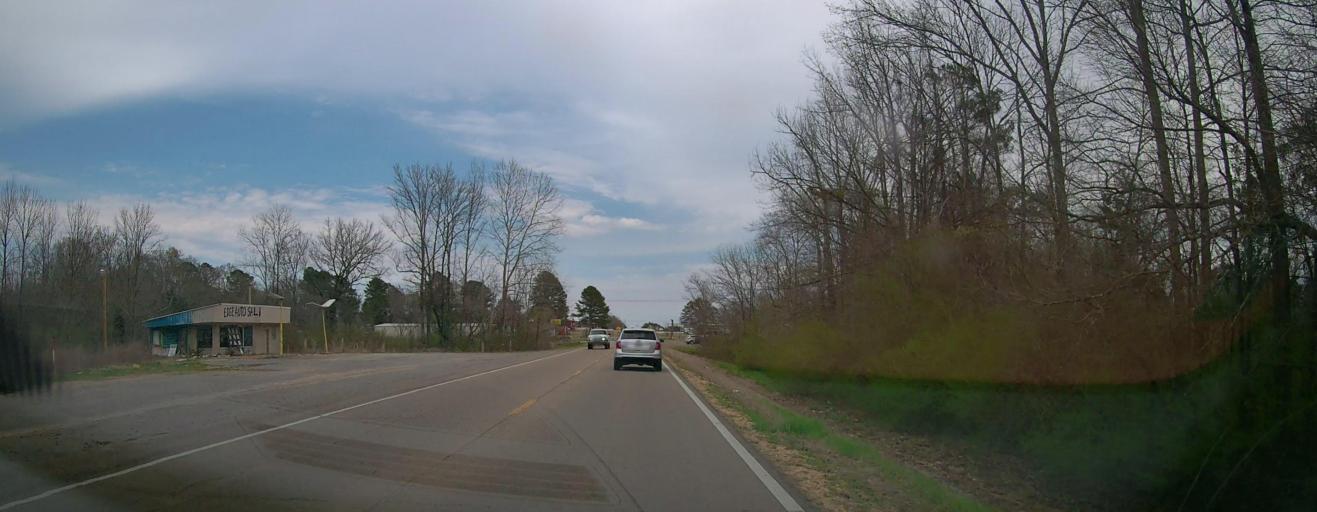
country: US
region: Mississippi
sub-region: Lee County
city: Plantersville
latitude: 34.2665
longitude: -88.5821
